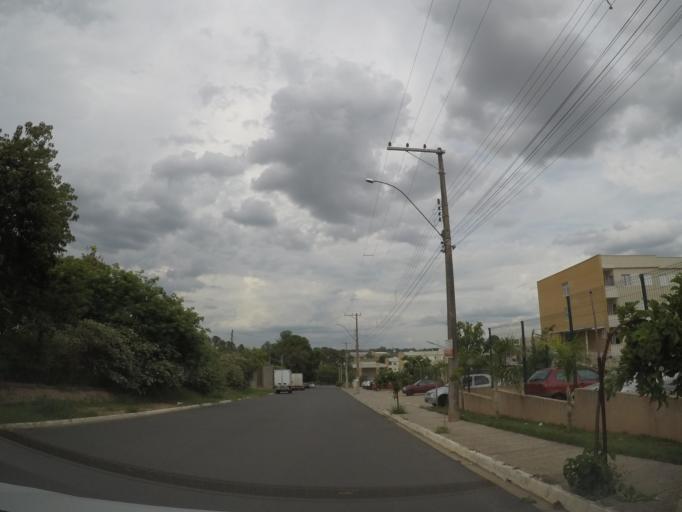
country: BR
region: Sao Paulo
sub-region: Sumare
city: Sumare
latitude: -22.8093
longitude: -47.2439
